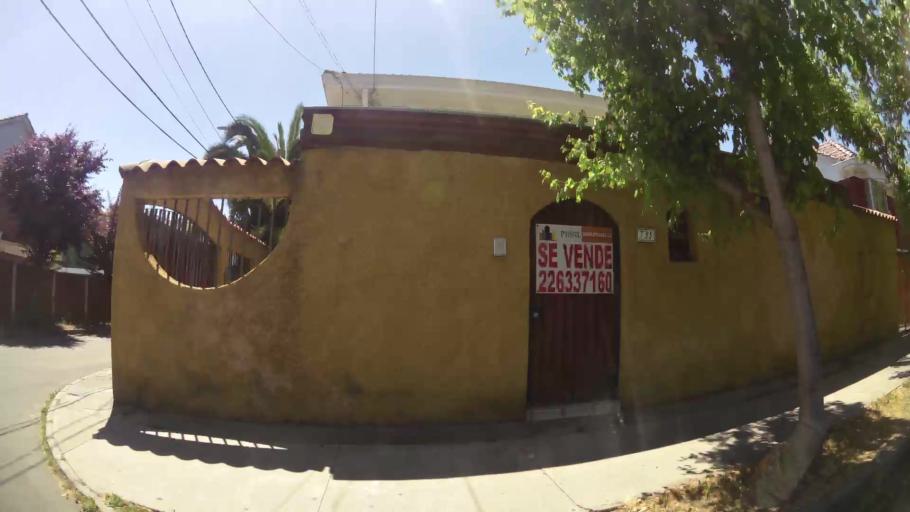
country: CL
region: Santiago Metropolitan
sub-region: Provincia de Maipo
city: San Bernardo
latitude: -33.6215
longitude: -70.7098
